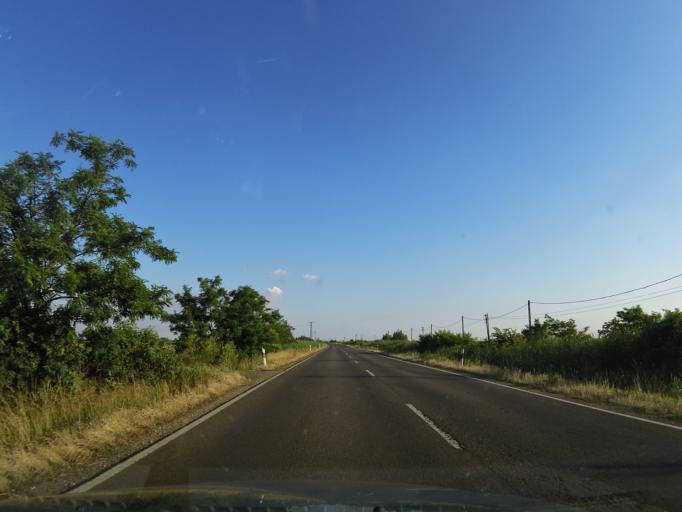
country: HU
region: Jasz-Nagykun-Szolnok
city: Tiszafoldvar
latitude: 46.9398
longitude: 20.2688
